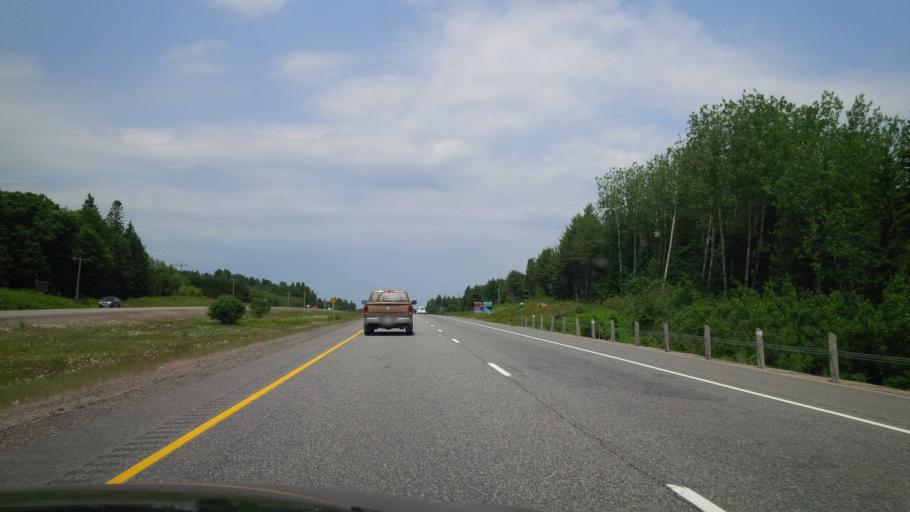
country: CA
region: Ontario
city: Huntsville
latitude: 45.4820
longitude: -79.2781
